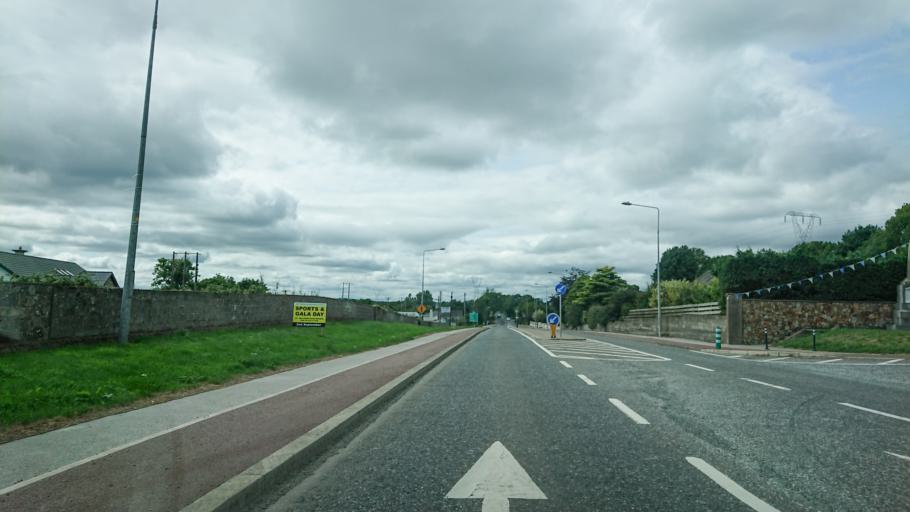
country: IE
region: Munster
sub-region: Waterford
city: Dungarvan
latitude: 52.1092
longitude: -7.6727
